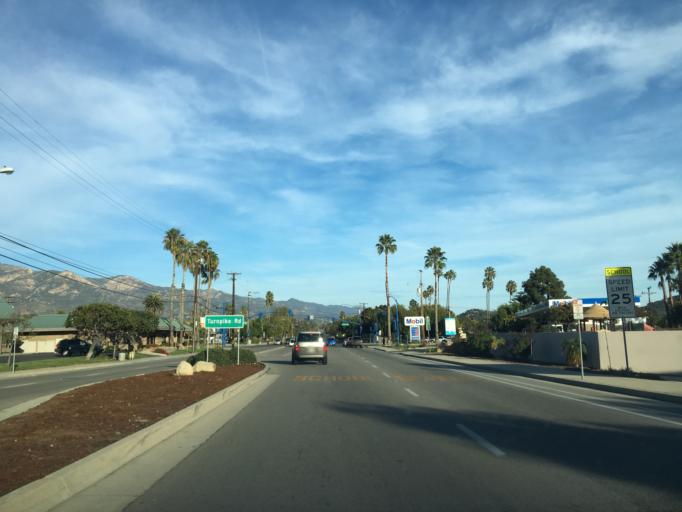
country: US
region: California
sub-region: Santa Barbara County
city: Goleta
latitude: 34.4362
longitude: -119.7912
